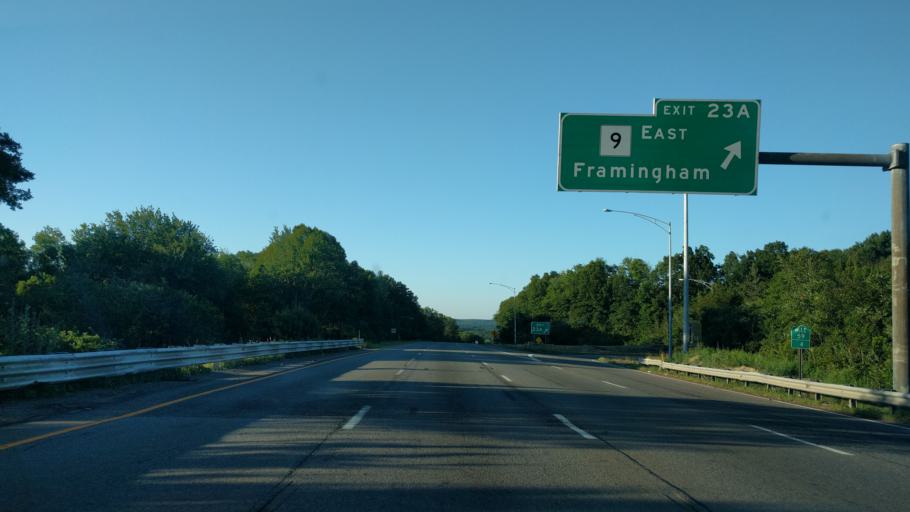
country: US
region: Massachusetts
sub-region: Worcester County
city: Southborough
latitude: 42.2882
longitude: -71.5675
